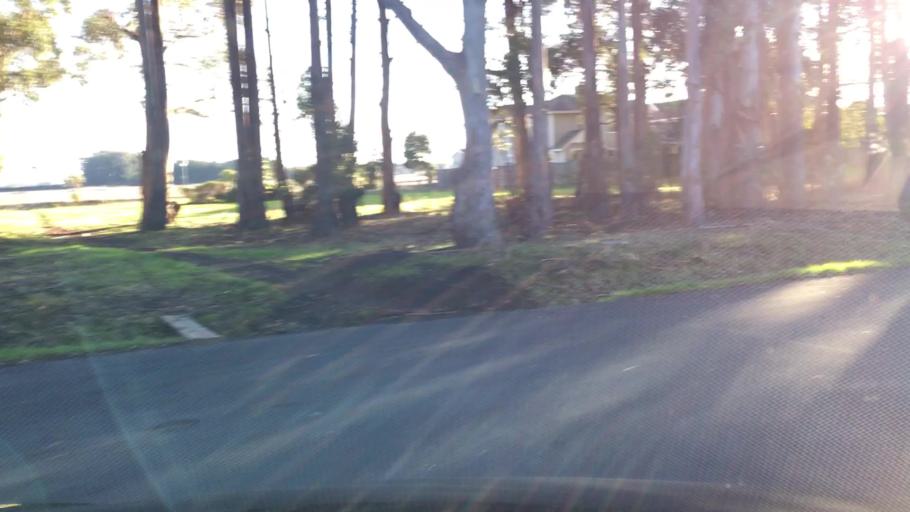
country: US
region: California
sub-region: San Mateo County
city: Half Moon Bay
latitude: 37.4543
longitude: -122.4343
